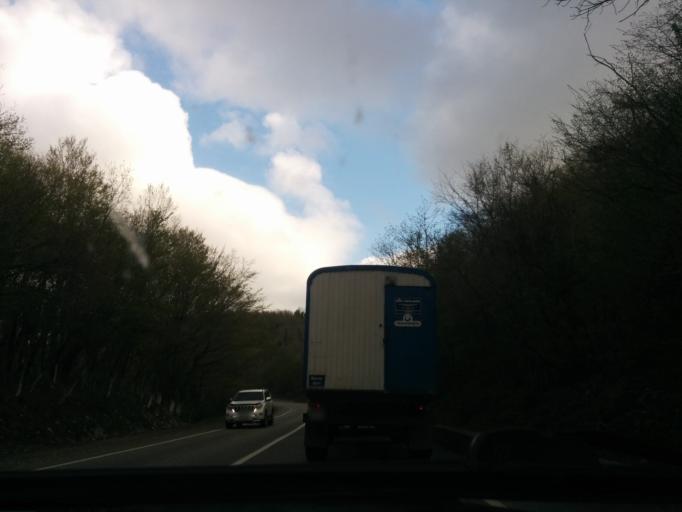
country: RU
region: Krasnodarskiy
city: Novomikhaylovskiy
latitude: 44.2543
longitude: 38.8822
